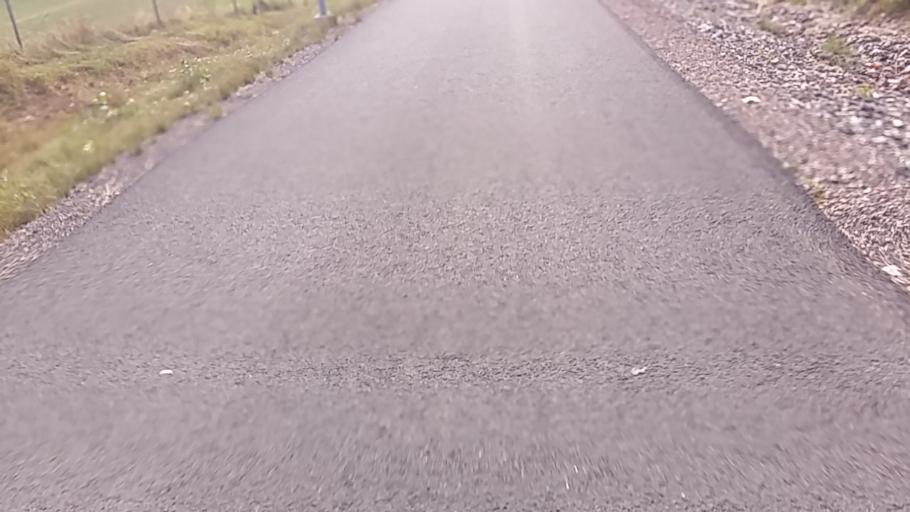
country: SE
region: Joenkoeping
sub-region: Jonkopings Kommun
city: Odensjo
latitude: 57.7315
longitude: 14.1452
